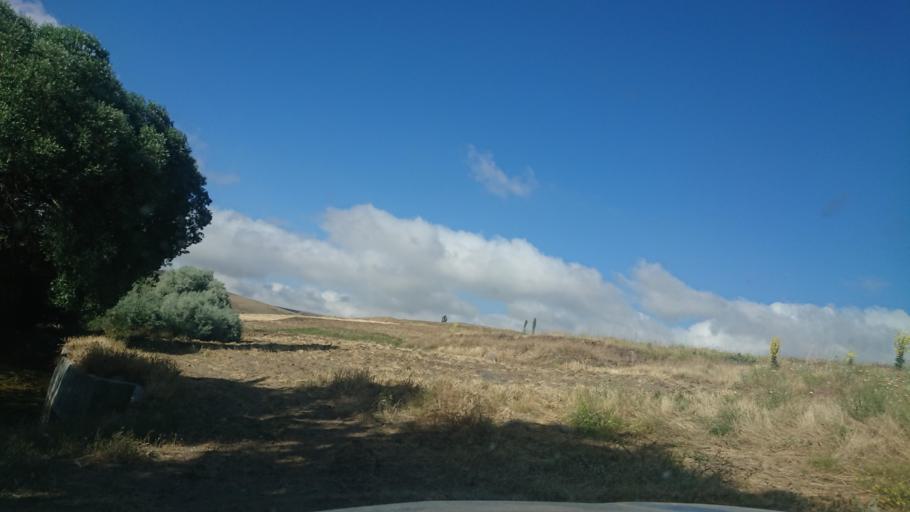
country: TR
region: Aksaray
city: Agacoren
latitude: 38.8490
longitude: 33.9286
